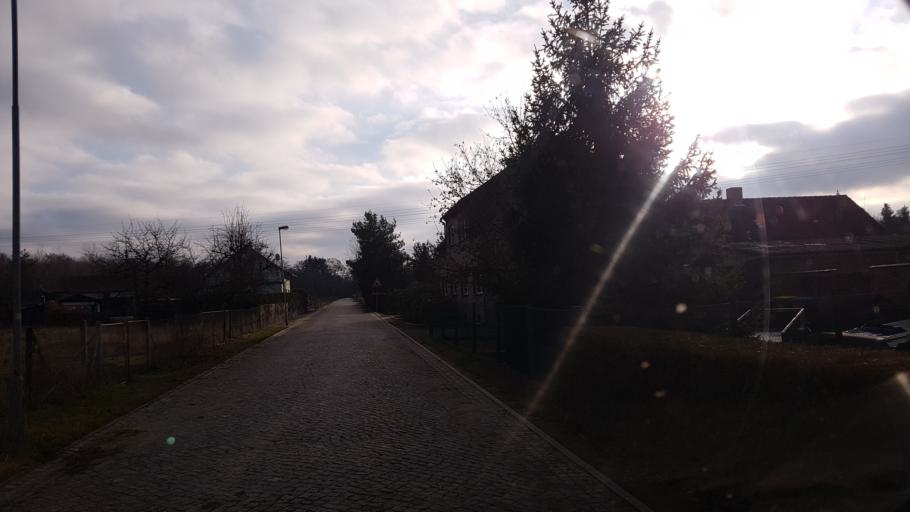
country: DE
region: Brandenburg
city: Sallgast
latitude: 51.5936
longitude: 13.7845
